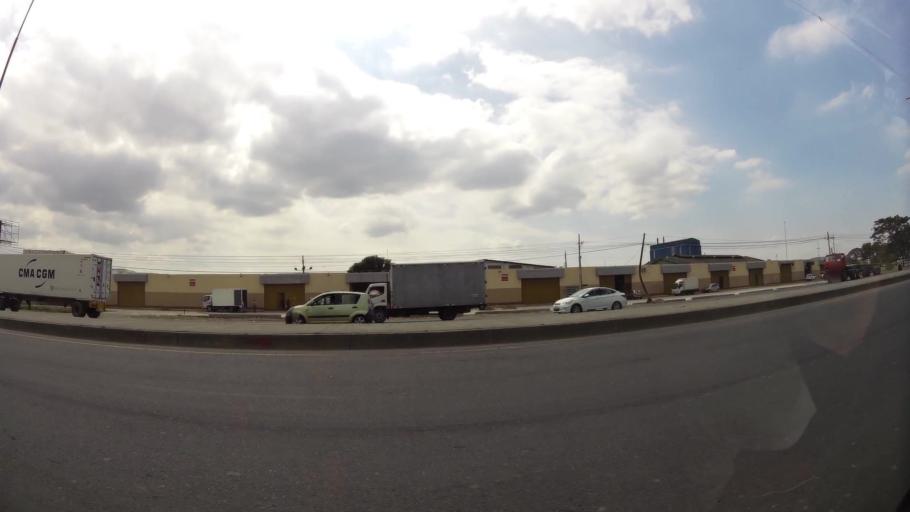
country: EC
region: Guayas
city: Santa Lucia
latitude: -2.0838
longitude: -79.9419
